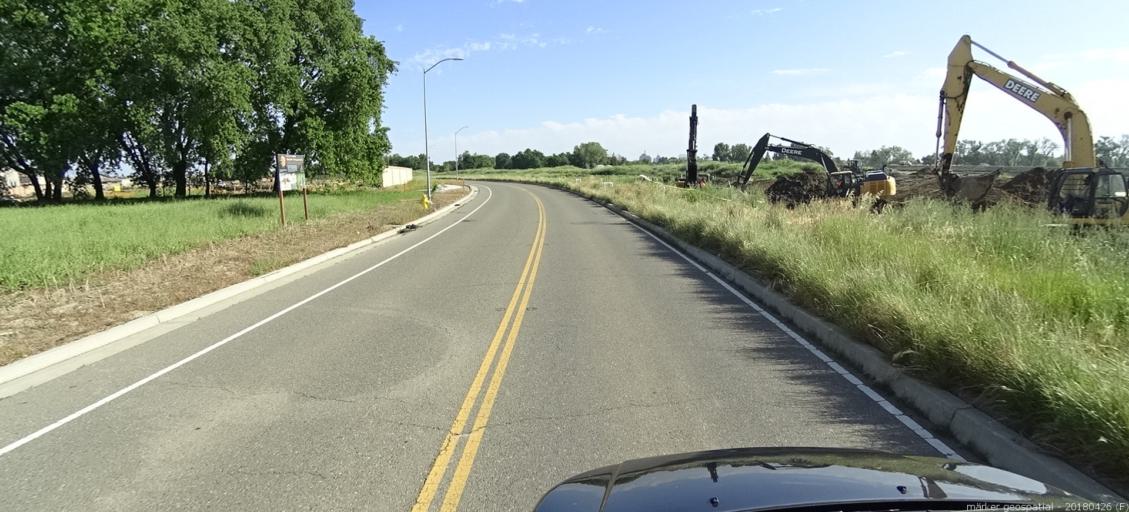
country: US
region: California
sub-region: Yolo County
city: West Sacramento
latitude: 38.5461
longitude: -121.5169
